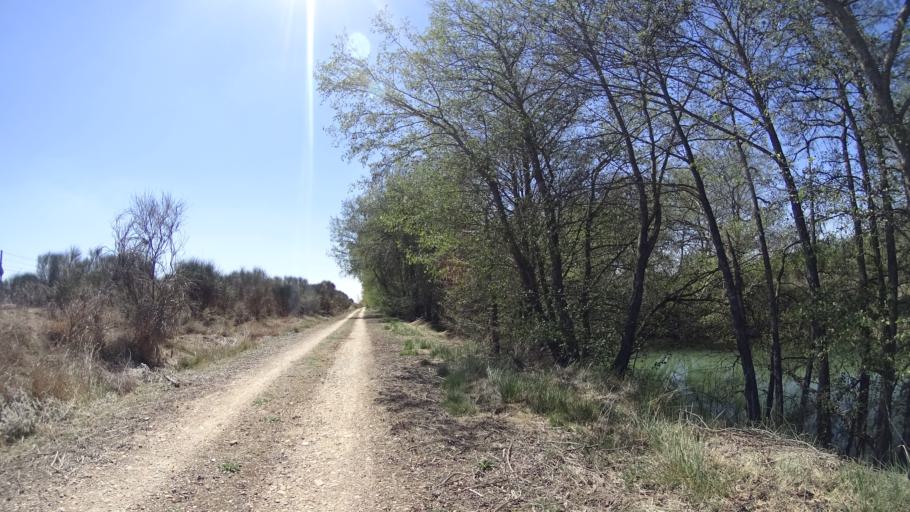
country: ES
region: Castille and Leon
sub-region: Provincia de Valladolid
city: Cubillas de Santa Marta
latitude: 41.7868
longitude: -4.6049
